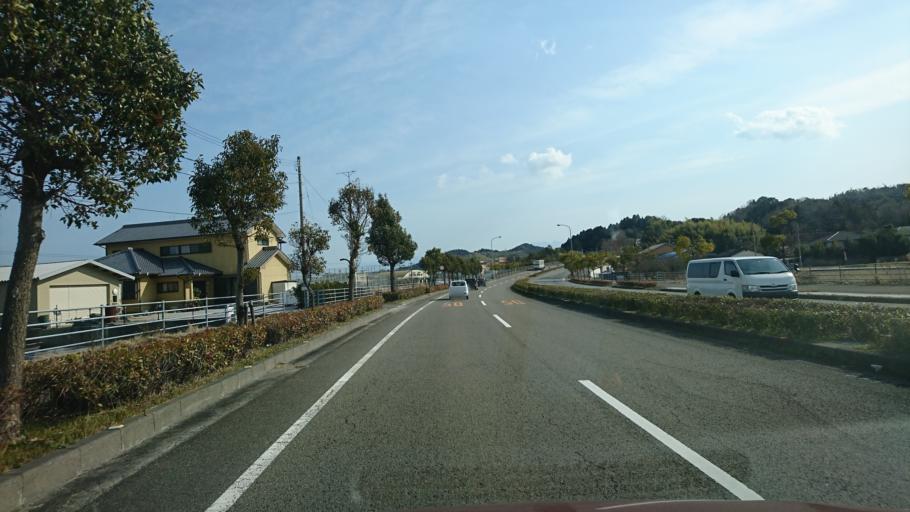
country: JP
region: Ehime
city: Saijo
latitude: 34.0186
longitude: 133.0293
